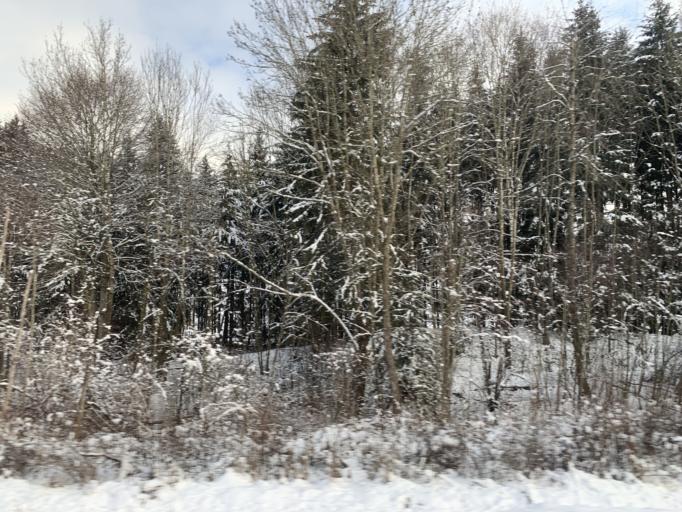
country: DE
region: Bavaria
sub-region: Swabia
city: Wildpoldsried
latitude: 47.7969
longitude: 10.3993
